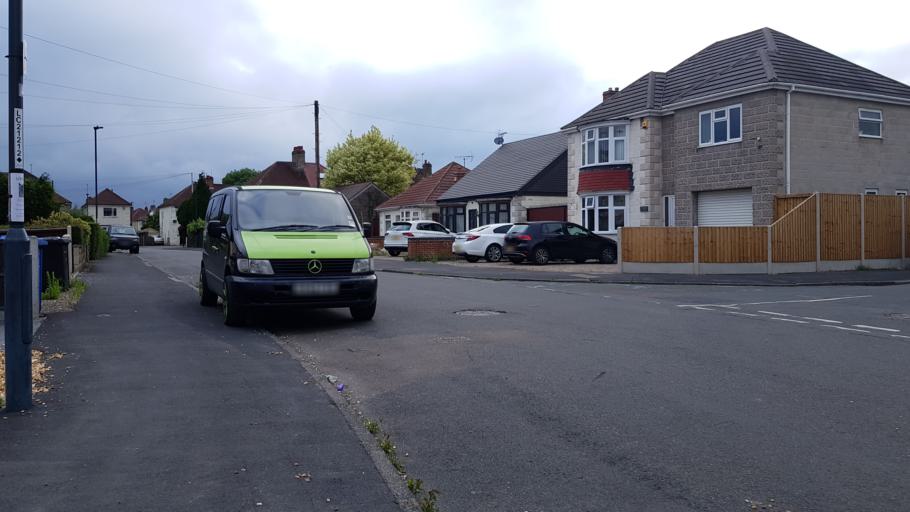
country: GB
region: England
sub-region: Derby
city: Derby
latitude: 52.8904
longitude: -1.4388
